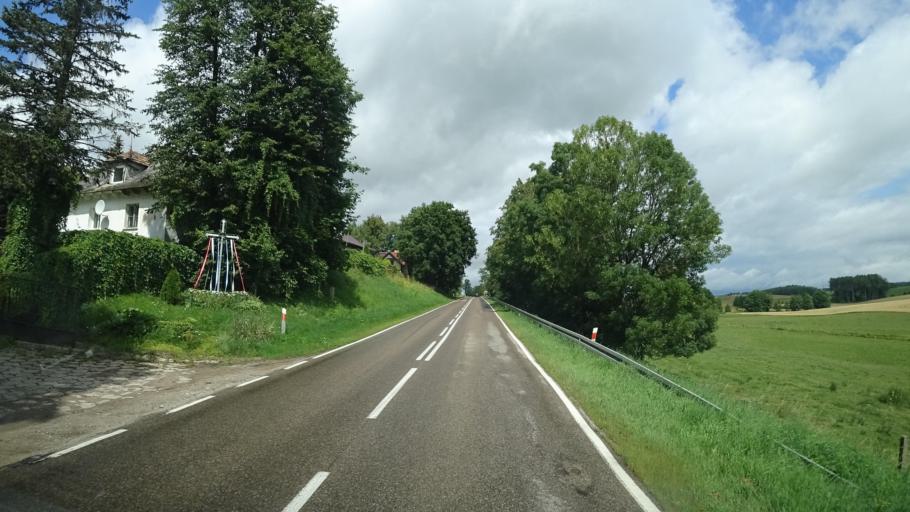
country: PL
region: Warmian-Masurian Voivodeship
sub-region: Powiat olecki
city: Kowale Oleckie
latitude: 54.1455
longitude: 22.4286
